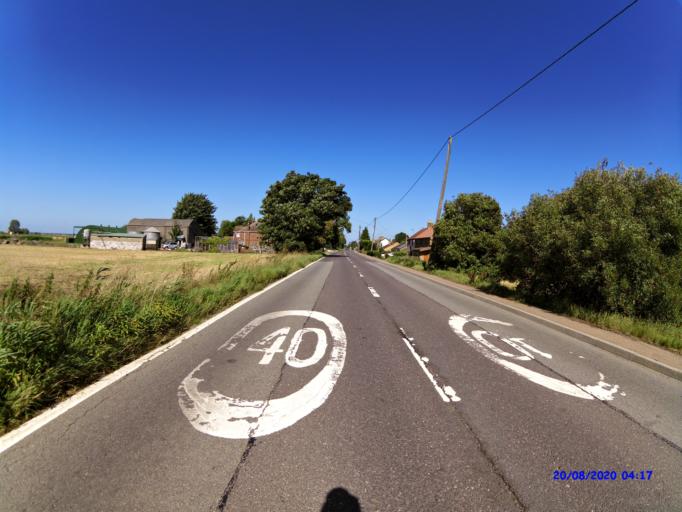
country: GB
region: England
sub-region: Cambridgeshire
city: Ramsey
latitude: 52.4897
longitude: -0.1151
